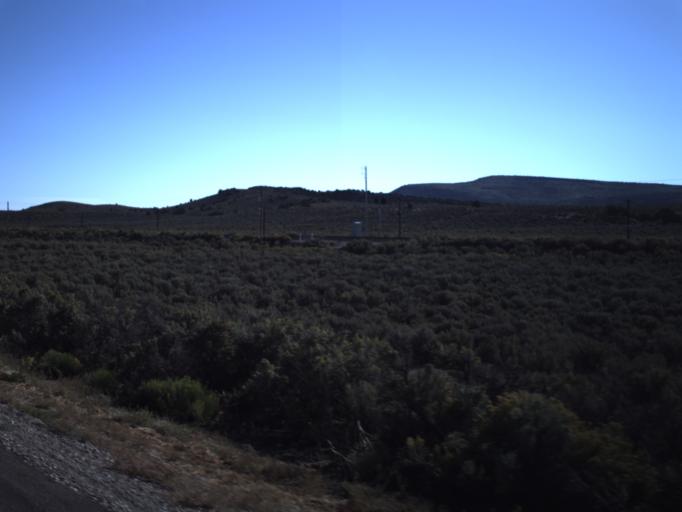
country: US
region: Utah
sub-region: Washington County
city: Enterprise
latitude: 37.7621
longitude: -113.9866
